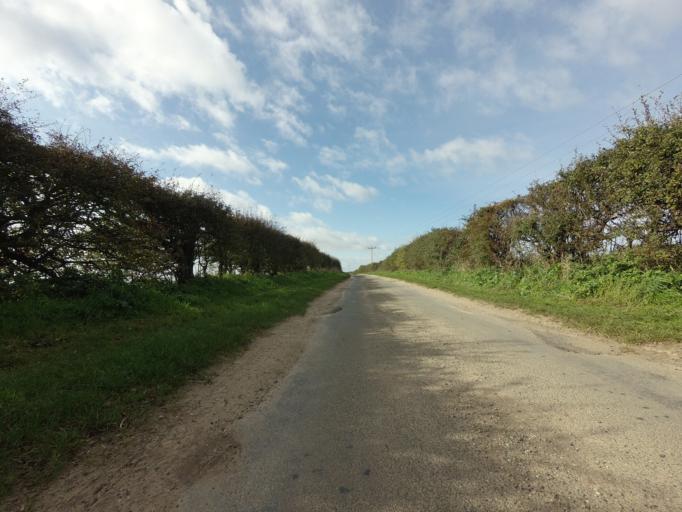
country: GB
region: England
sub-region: Norfolk
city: Hunstanton
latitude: 52.9354
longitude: 0.6453
